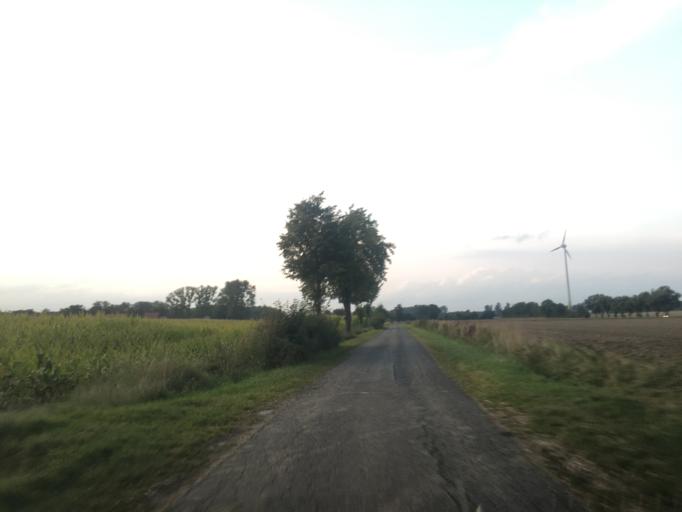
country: DE
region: North Rhine-Westphalia
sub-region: Regierungsbezirk Munster
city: Altenberge
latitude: 52.0006
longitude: 7.5256
